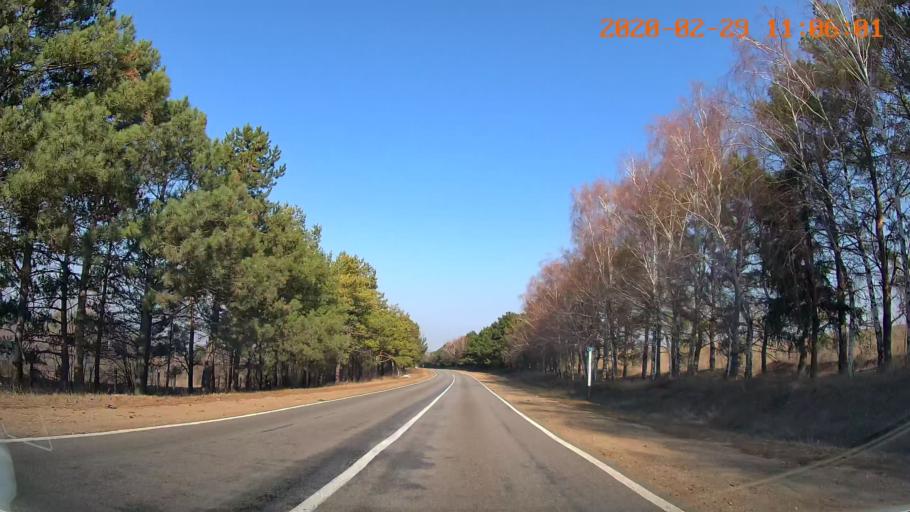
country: MD
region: Criuleni
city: Criuleni
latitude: 47.2093
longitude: 29.1898
